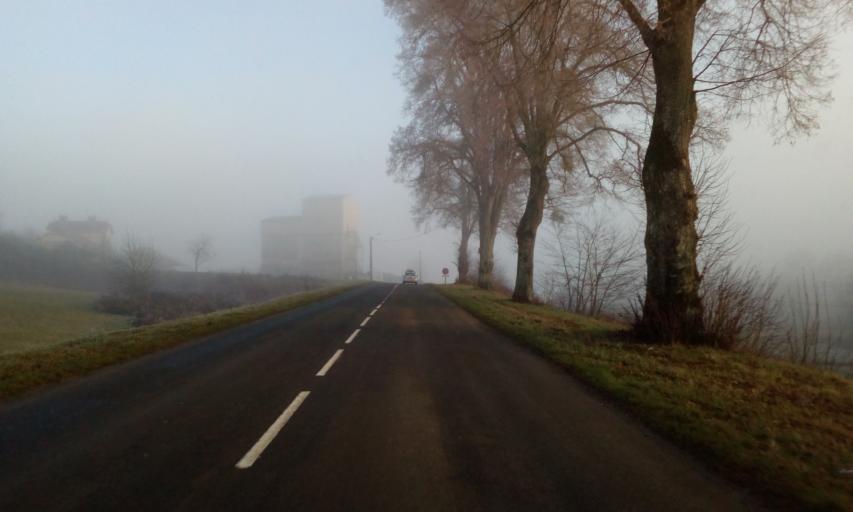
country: FR
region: Champagne-Ardenne
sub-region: Departement des Ardennes
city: Rimogne
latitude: 49.7774
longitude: 4.4425
